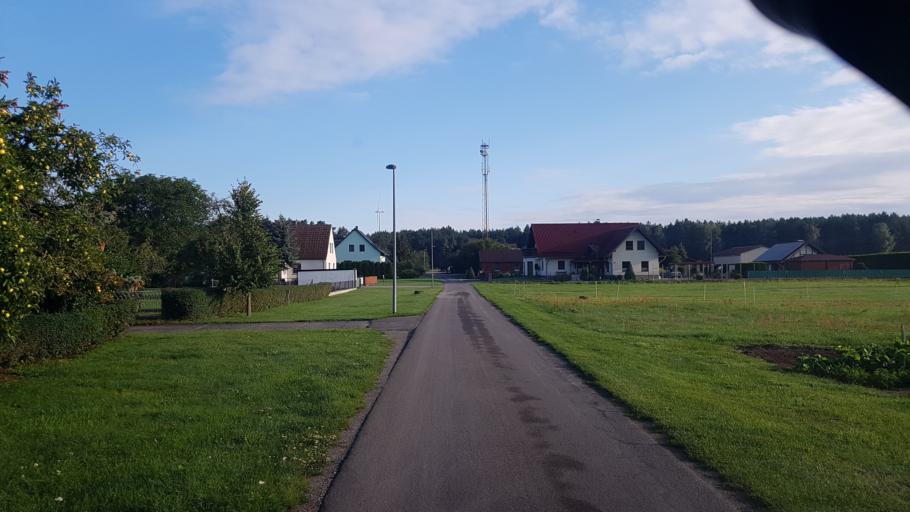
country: DE
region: Brandenburg
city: Bronkow
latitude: 51.6736
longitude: 13.8916
